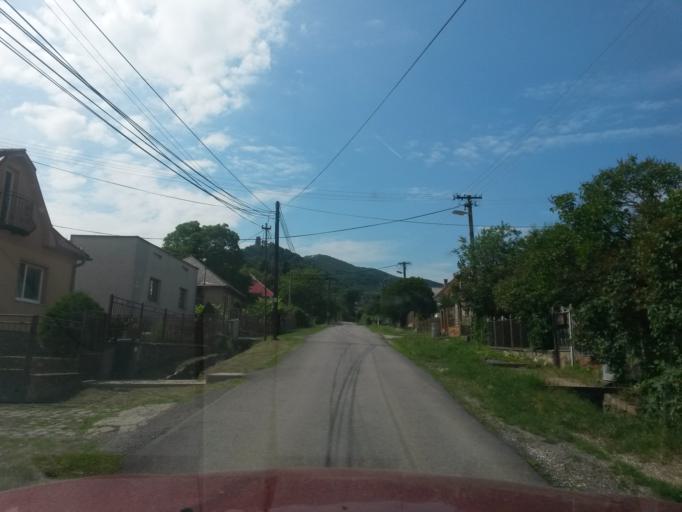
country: SK
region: Kosicky
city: Secovce
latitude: 48.6321
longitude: 21.4832
